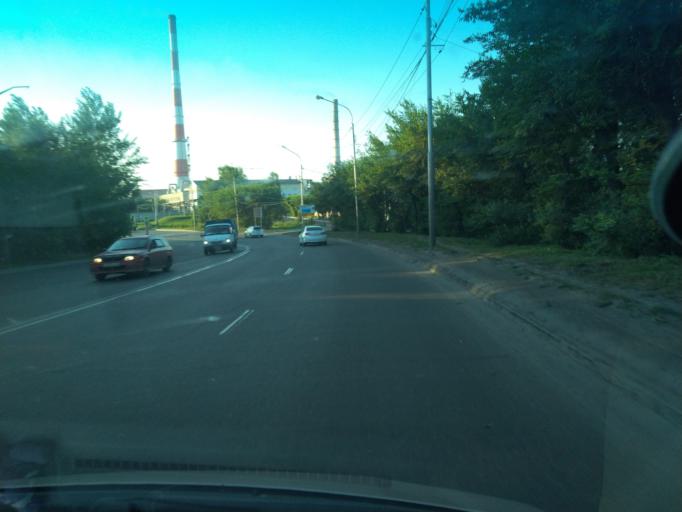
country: RU
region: Krasnoyarskiy
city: Berezovka
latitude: 56.0174
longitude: 93.0318
